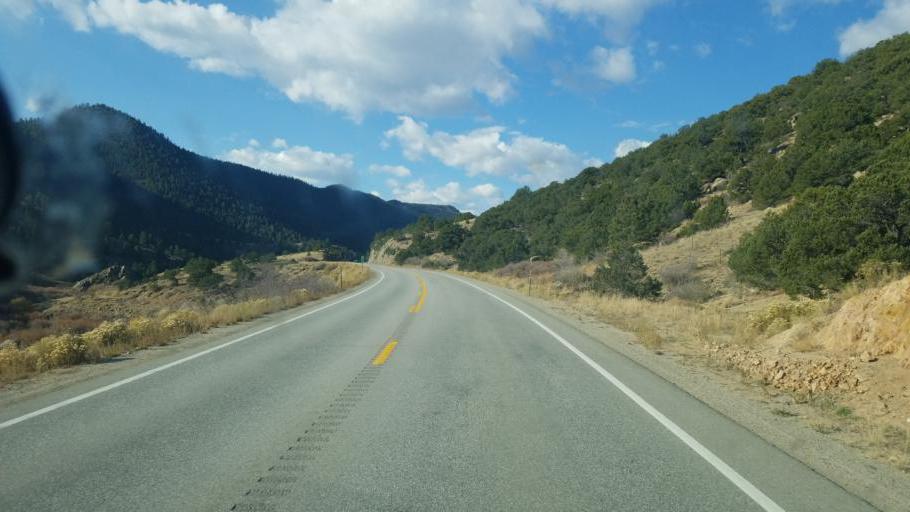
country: US
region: Colorado
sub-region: Chaffee County
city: Buena Vista
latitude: 38.8402
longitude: -106.0143
